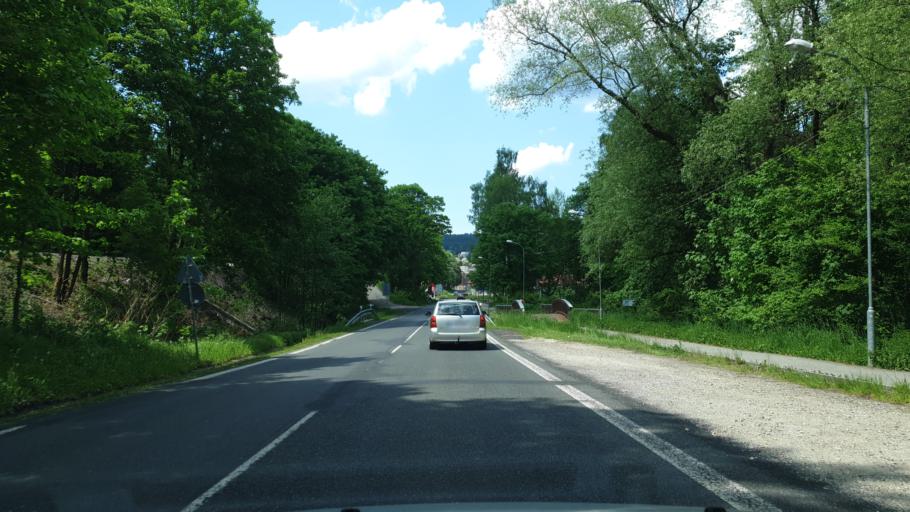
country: DE
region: Saxony
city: Klingenthal
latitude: 50.3508
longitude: 12.4737
